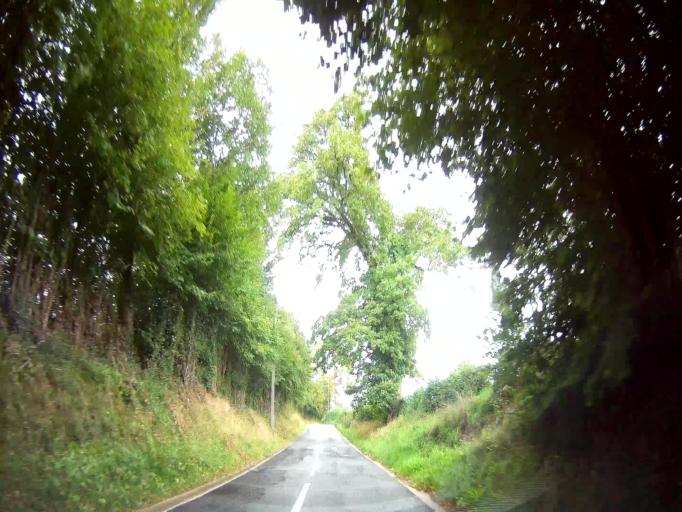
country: BE
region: Wallonia
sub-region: Province de Liege
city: Limbourg
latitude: 50.6073
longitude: 5.9375
